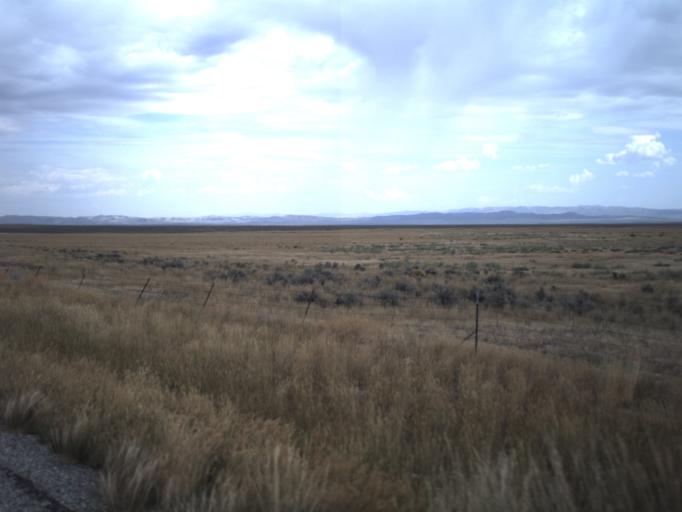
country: US
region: Idaho
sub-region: Oneida County
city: Malad City
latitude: 41.9197
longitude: -113.0958
